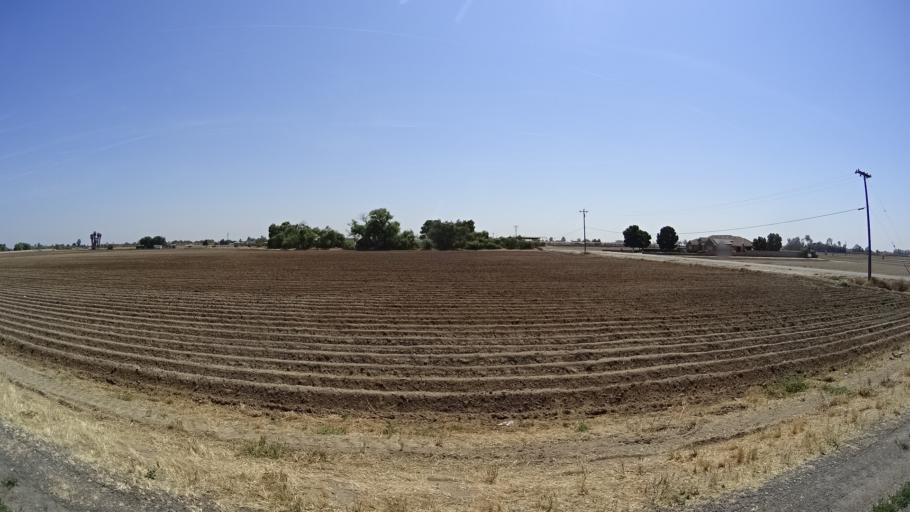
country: US
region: California
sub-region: Fresno County
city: Riverdale
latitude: 36.3806
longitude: -119.8514
